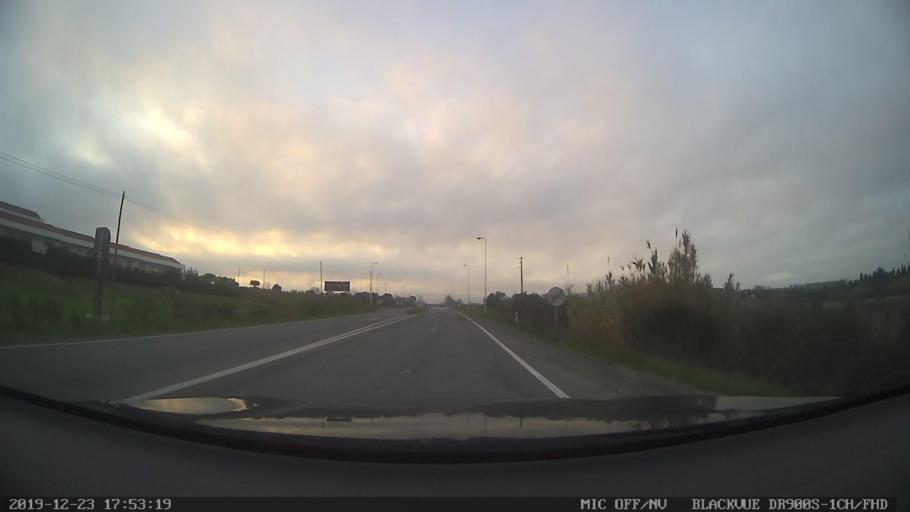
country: PT
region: Aveiro
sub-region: Mealhada
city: Mealhada
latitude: 40.3731
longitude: -8.4809
